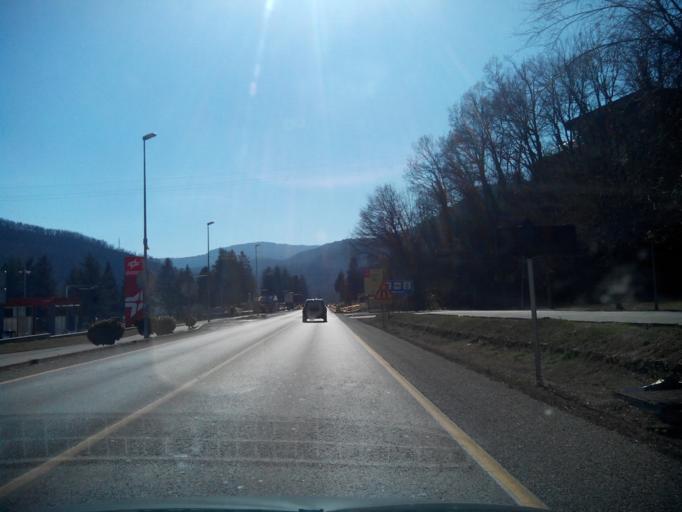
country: ES
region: Catalonia
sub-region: Provincia de Girona
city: Ripoll
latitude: 42.1856
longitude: 2.1964
